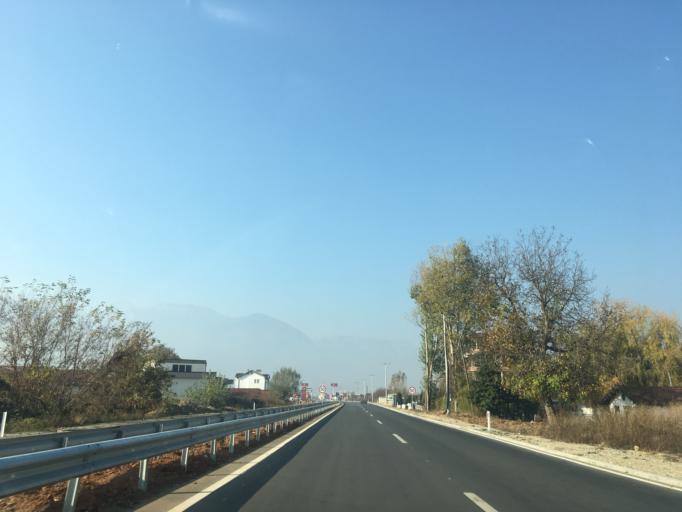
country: XK
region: Pec
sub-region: Komuna e Pejes
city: Dubova (Driloni)
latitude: 42.6584
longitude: 20.3489
